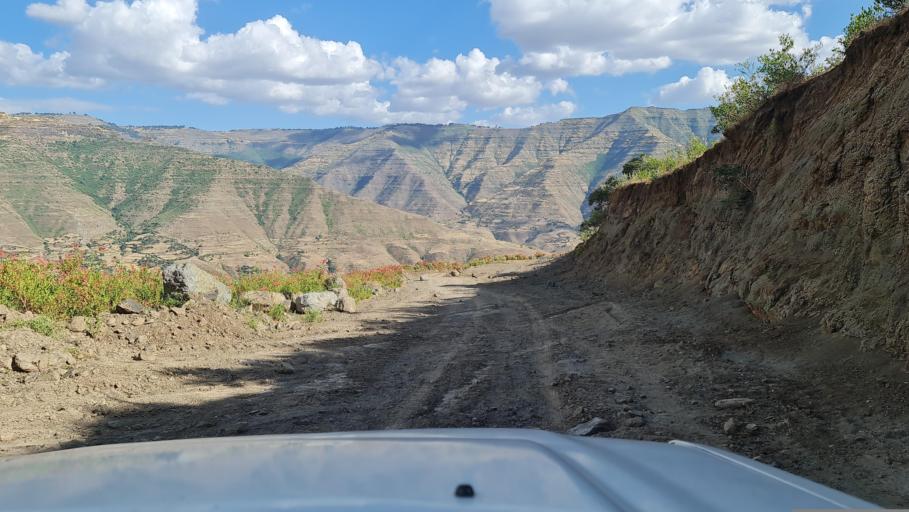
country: ET
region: Amhara
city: Debark'
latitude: 13.1239
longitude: 38.0197
